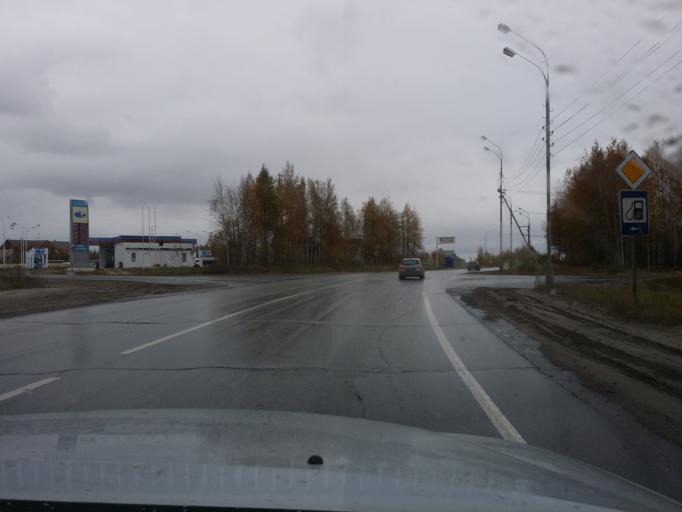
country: RU
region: Khanty-Mansiyskiy Avtonomnyy Okrug
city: Megion
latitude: 61.0494
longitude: 76.1121
